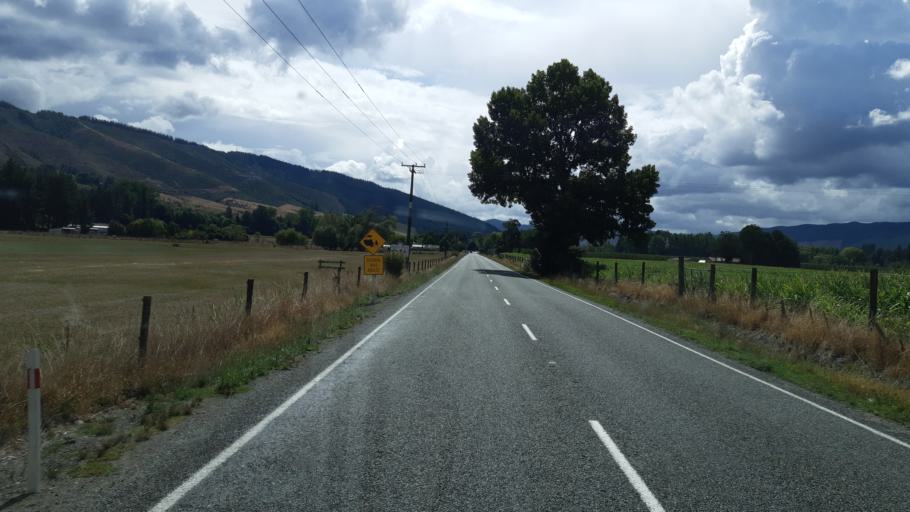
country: NZ
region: Tasman
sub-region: Tasman District
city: Wakefield
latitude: -41.4656
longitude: 172.8087
